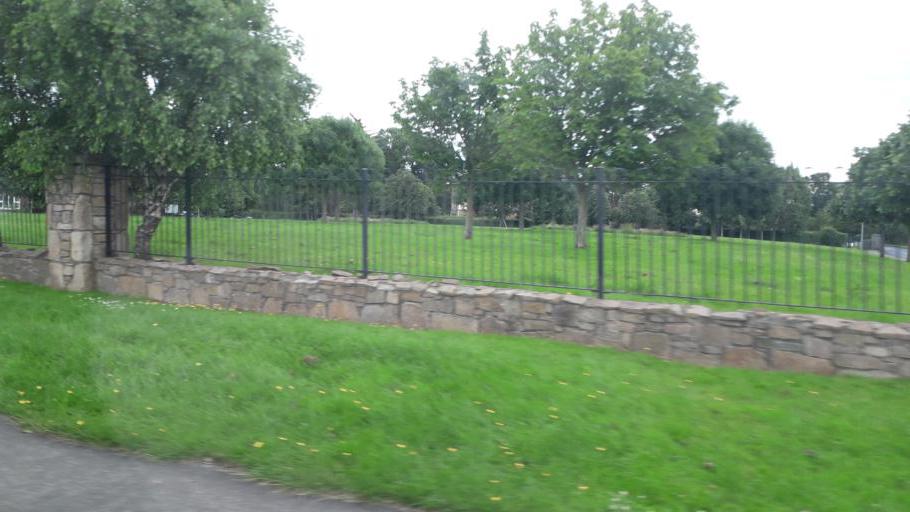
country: IE
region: Leinster
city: Templeogue
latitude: 53.3099
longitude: -6.3121
